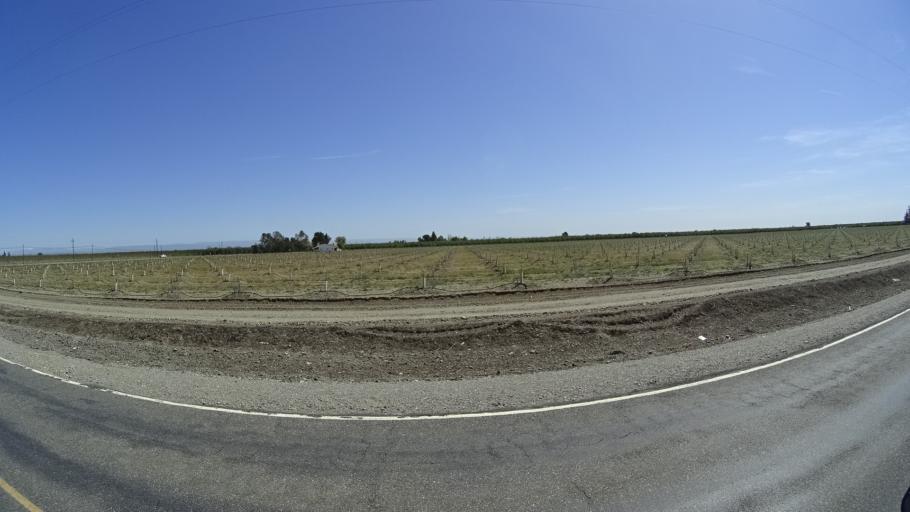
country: US
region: California
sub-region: Glenn County
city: Orland
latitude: 39.7093
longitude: -122.1406
